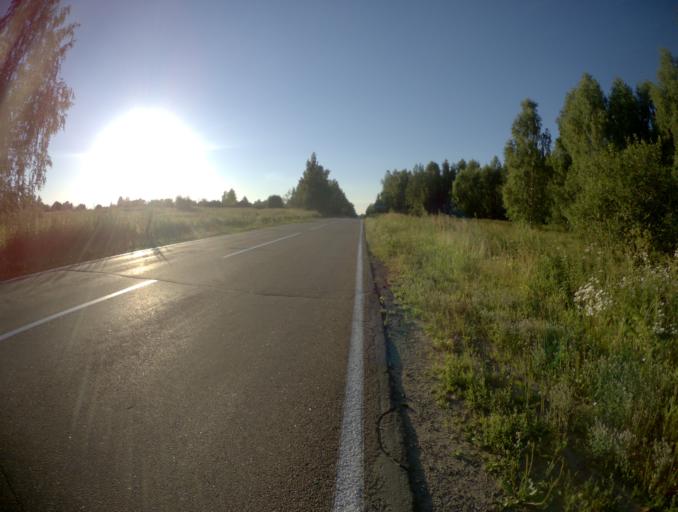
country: RU
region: Vladimir
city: Galitsy
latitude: 56.1508
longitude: 42.8599
